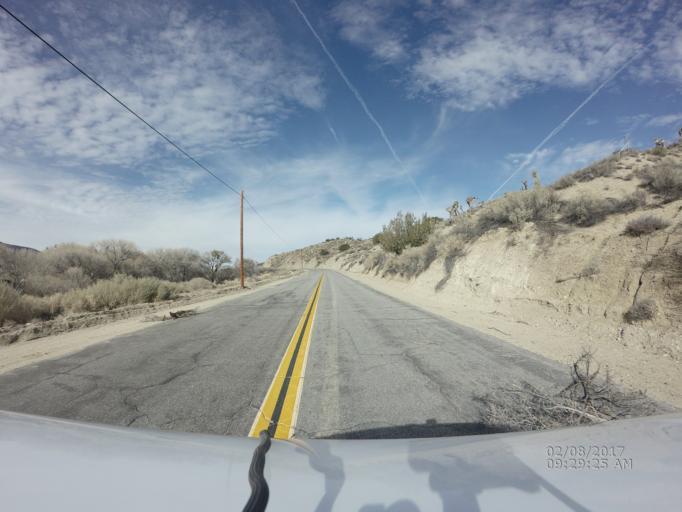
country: US
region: California
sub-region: Los Angeles County
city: Littlerock
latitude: 34.4561
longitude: -117.8841
